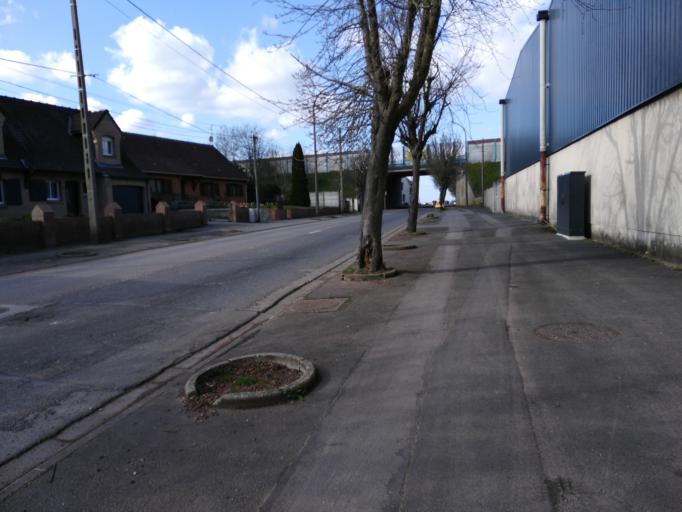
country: FR
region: Nord-Pas-de-Calais
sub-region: Departement du Pas-de-Calais
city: Montigny-en-Gohelle
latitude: 50.4315
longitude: 2.9462
